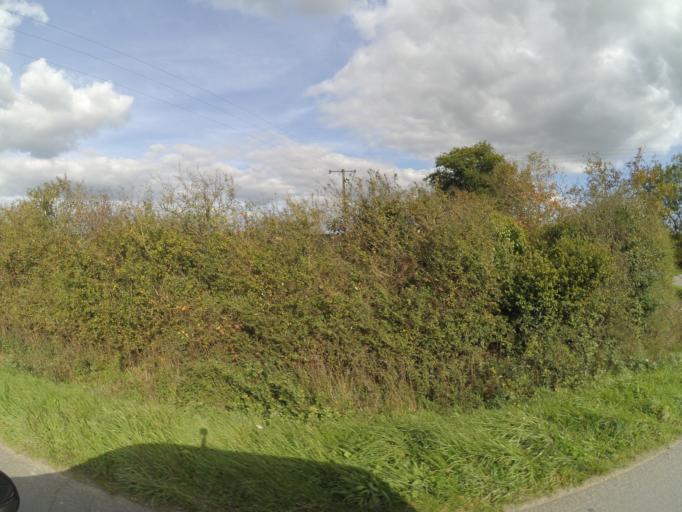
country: FR
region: Pays de la Loire
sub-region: Departement de la Loire-Atlantique
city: Casson
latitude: 47.4076
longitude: -1.5933
